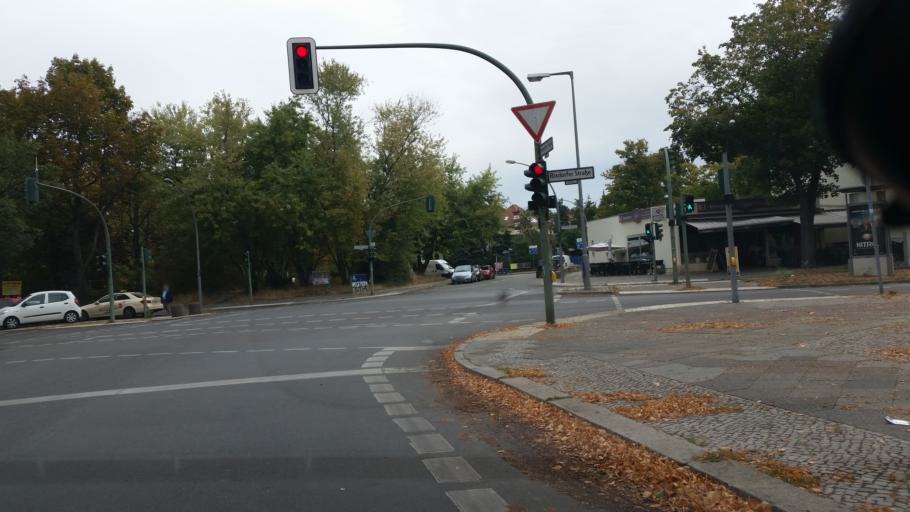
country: DE
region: Berlin
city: Tempelhof Bezirk
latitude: 52.4468
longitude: 13.4016
